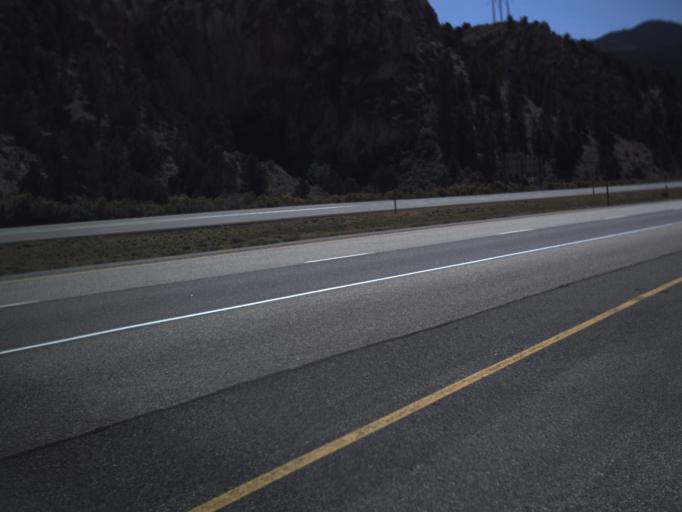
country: US
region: Utah
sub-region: Sevier County
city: Monroe
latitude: 38.5680
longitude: -112.3526
